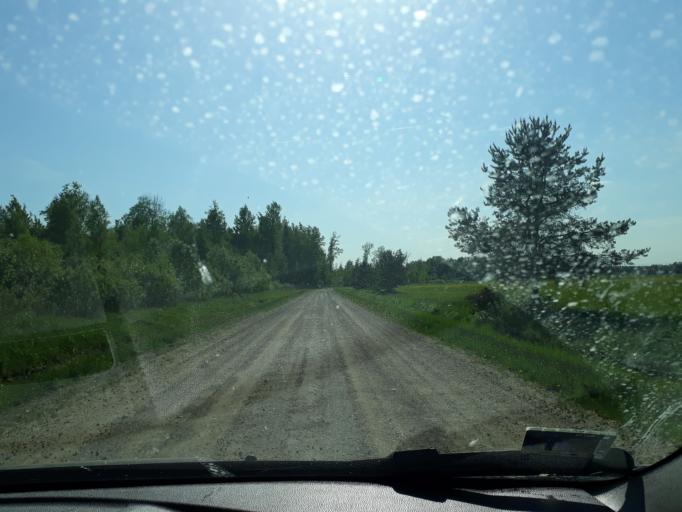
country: EE
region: Paernumaa
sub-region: Tootsi vald
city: Tootsi
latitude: 58.5805
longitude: 24.9208
